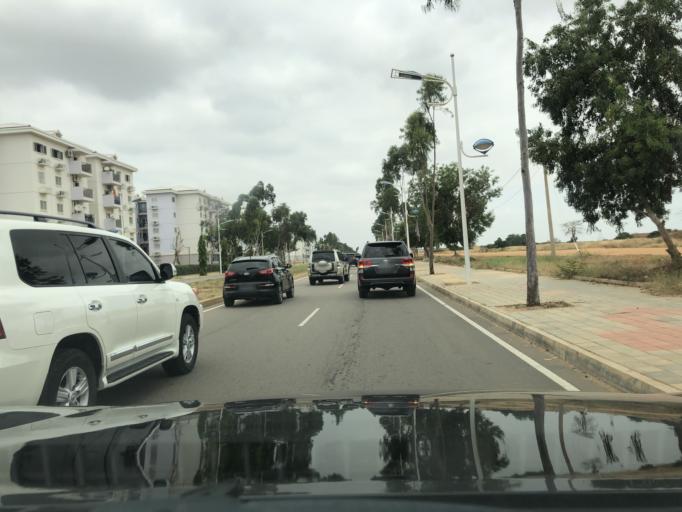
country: AO
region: Luanda
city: Luanda
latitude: -8.9911
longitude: 13.2792
